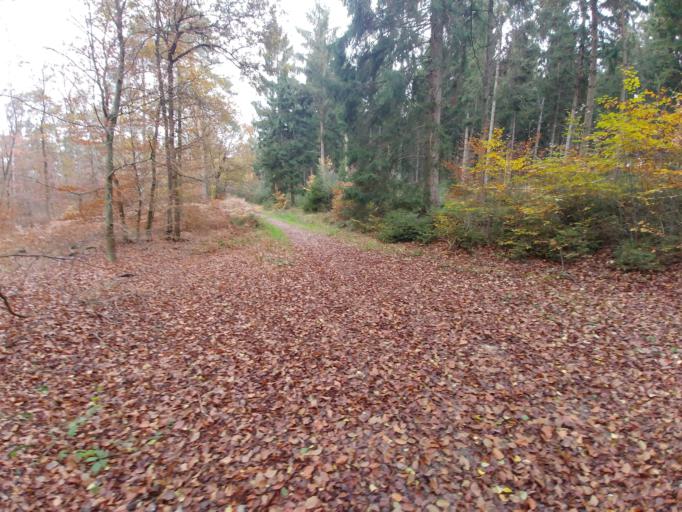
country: NL
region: Utrecht
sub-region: Gemeente Utrechtse Heuvelrug
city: Amerongen
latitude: 52.0097
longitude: 5.4818
